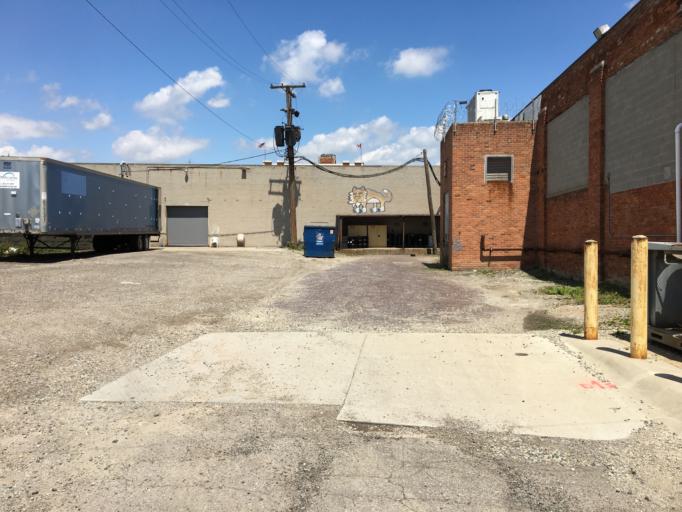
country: US
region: Michigan
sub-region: Wayne County
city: Detroit
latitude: 42.3217
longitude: -83.0688
